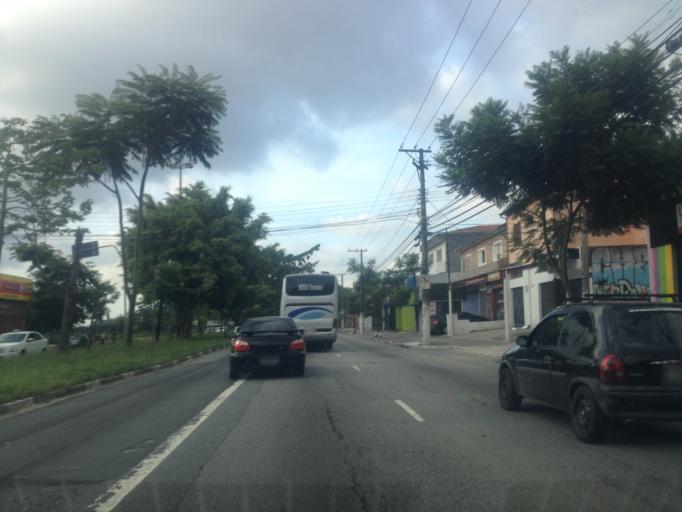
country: BR
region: Sao Paulo
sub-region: Diadema
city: Diadema
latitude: -23.6924
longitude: -46.7147
